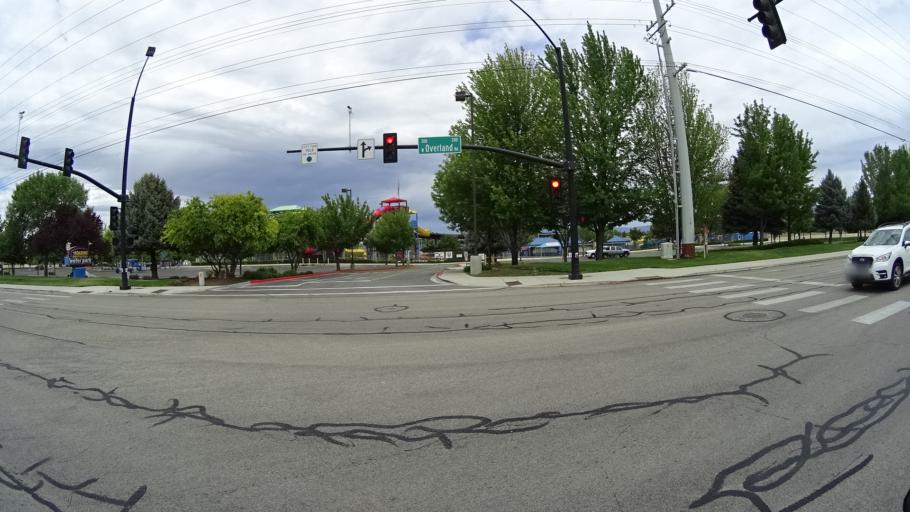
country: US
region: Idaho
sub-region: Ada County
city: Meridian
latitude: 43.5900
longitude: -116.3986
